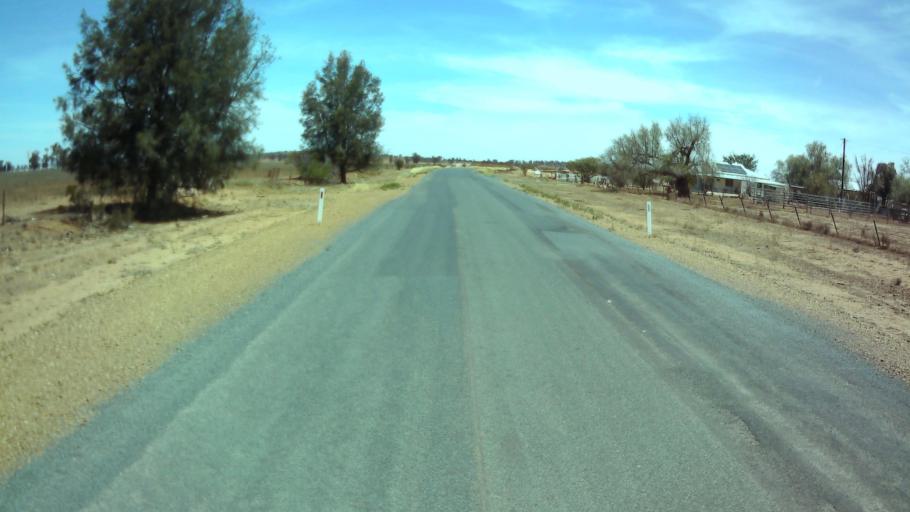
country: AU
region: New South Wales
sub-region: Weddin
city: Grenfell
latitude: -33.7494
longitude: 147.7673
